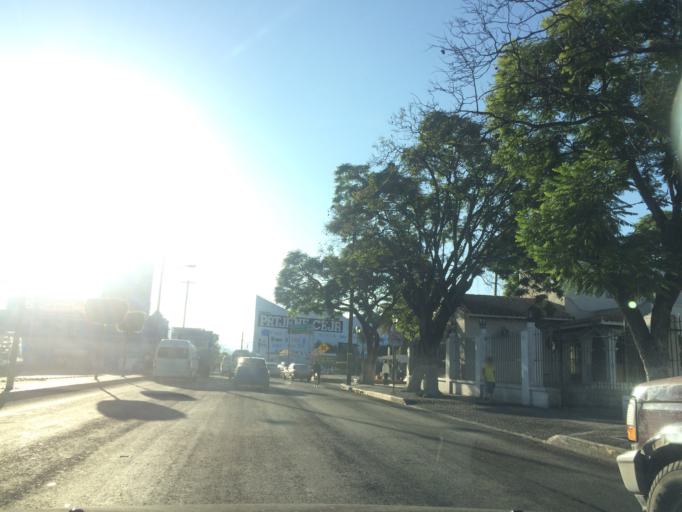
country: MX
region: Puebla
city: Tehuacan
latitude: 18.4633
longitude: -97.4020
